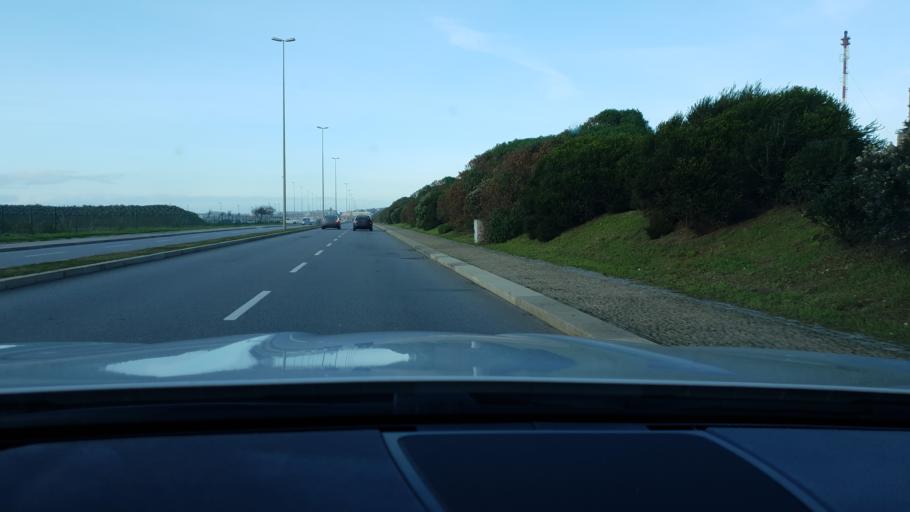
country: PT
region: Porto
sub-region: Matosinhos
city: Leca da Palmeira
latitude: 41.2130
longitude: -8.7132
